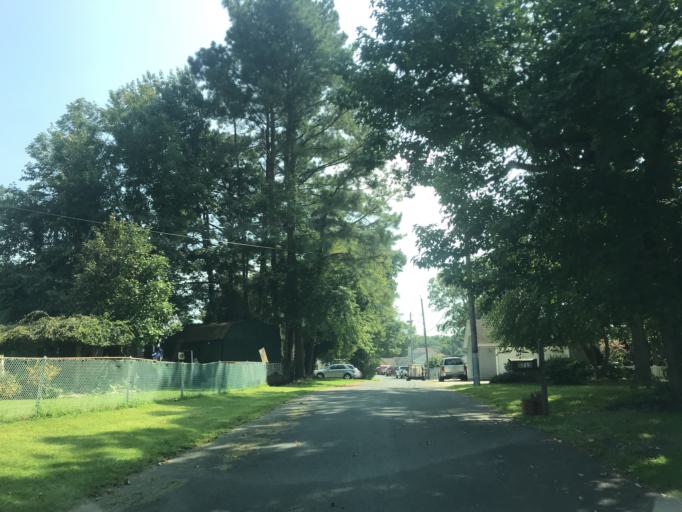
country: US
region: Maryland
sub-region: Baltimore County
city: Bowleys Quarters
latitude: 39.3754
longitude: -76.3701
